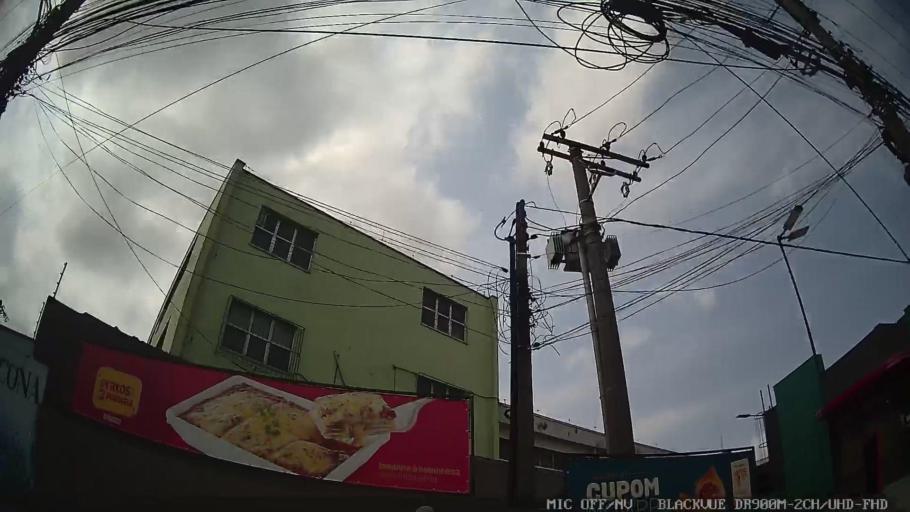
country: BR
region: Sao Paulo
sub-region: Taboao Da Serra
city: Taboao da Serra
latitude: -23.6662
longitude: -46.7181
